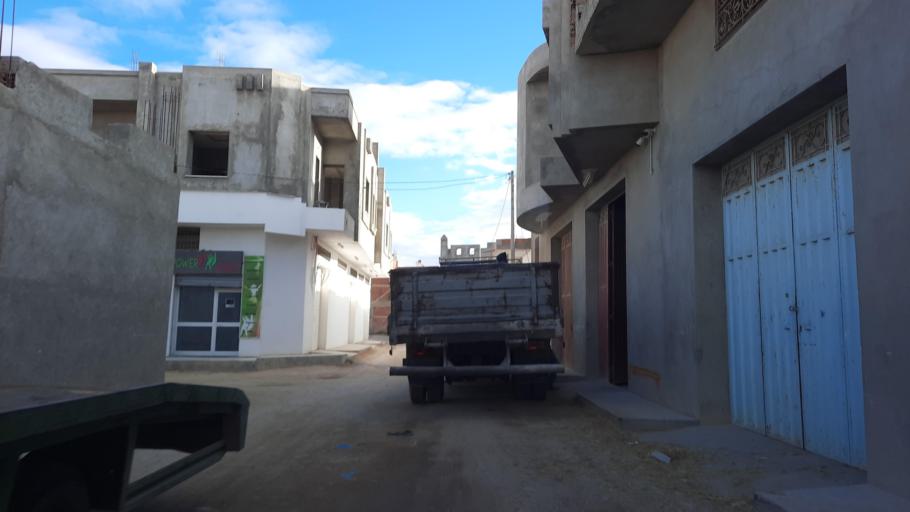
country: TN
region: Al Mahdiyah
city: El Jem
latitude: 35.2921
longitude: 10.7032
